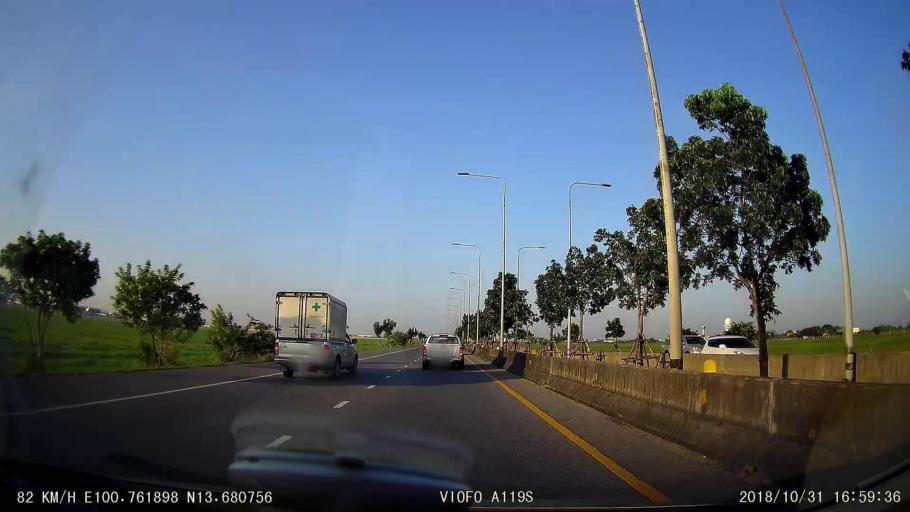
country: TH
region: Bangkok
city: Lat Krabang
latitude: 13.6809
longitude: 100.7619
